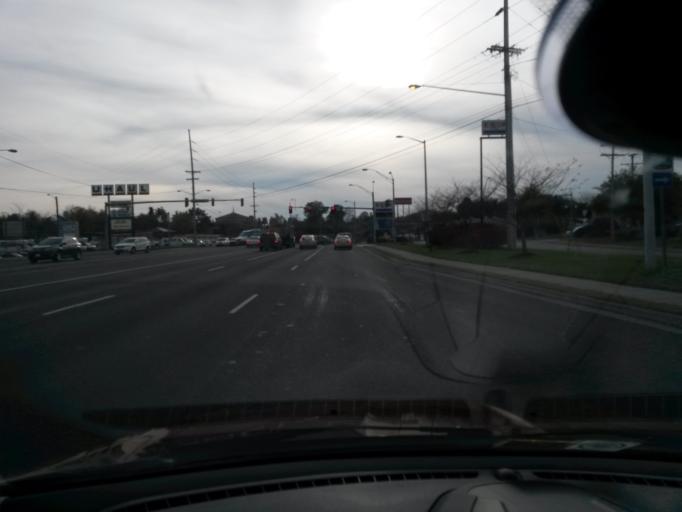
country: US
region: Virginia
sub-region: Roanoke County
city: Hollins
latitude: 37.3066
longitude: -79.9772
